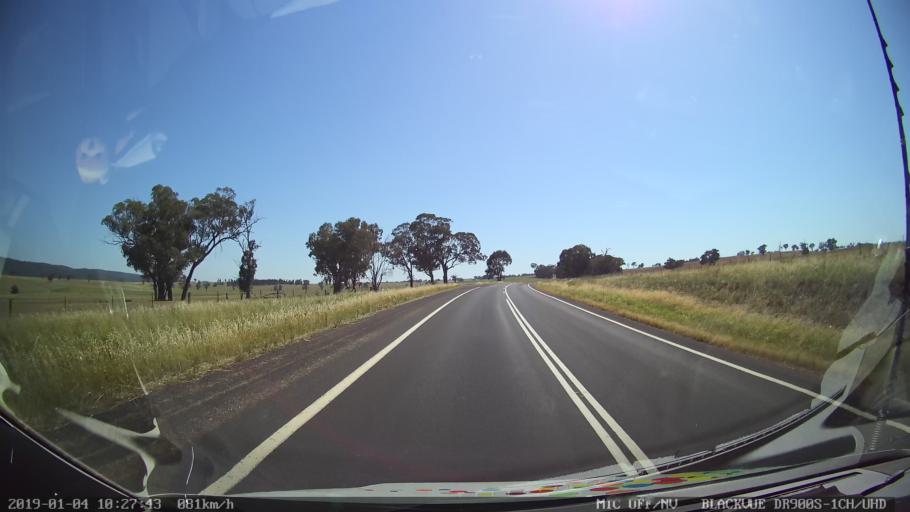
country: AU
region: New South Wales
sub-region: Cabonne
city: Canowindra
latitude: -33.3675
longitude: 148.6013
